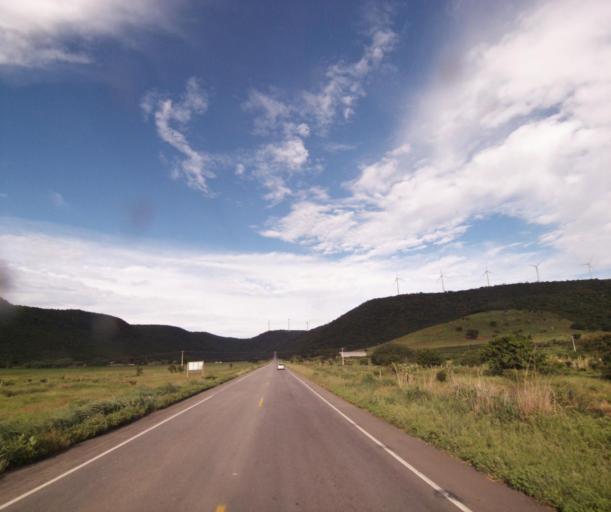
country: BR
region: Bahia
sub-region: Guanambi
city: Guanambi
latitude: -14.1596
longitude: -42.7119
